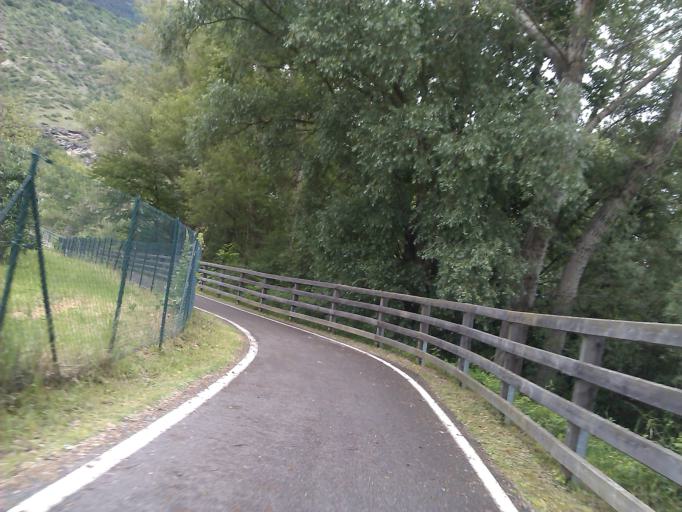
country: IT
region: Trentino-Alto Adige
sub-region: Bolzano
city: Laces
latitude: 46.6183
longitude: 10.8405
